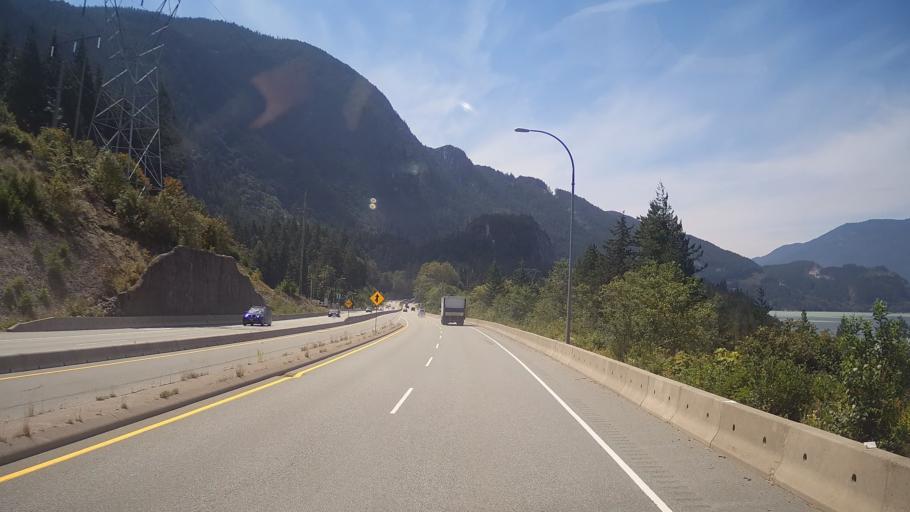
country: CA
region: British Columbia
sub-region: Greater Vancouver Regional District
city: Lions Bay
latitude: 49.6782
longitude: -123.1568
